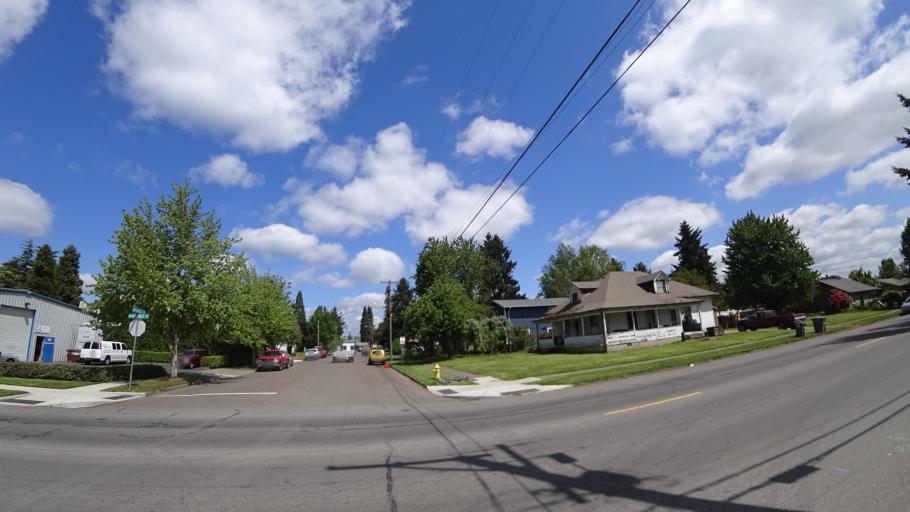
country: US
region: Oregon
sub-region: Washington County
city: Hillsboro
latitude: 45.5175
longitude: -122.9929
